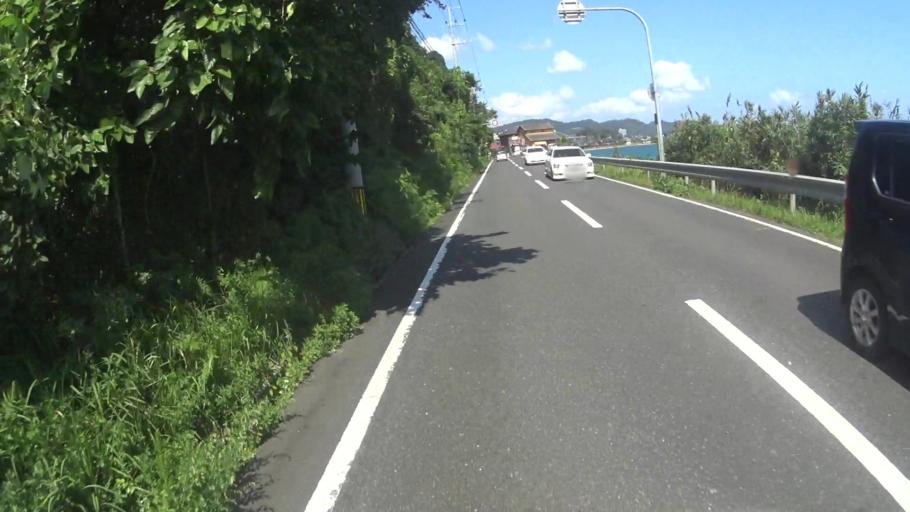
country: JP
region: Kyoto
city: Miyazu
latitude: 35.5941
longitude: 135.2124
